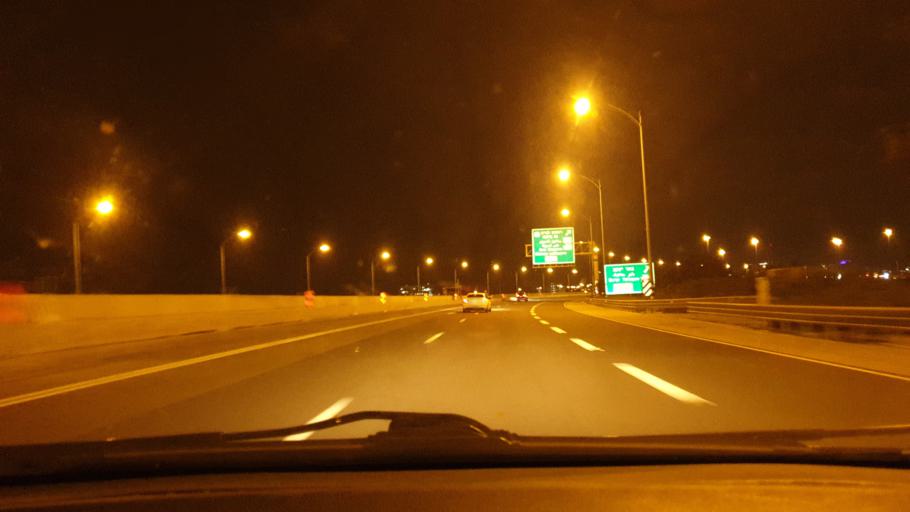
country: IL
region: Central District
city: Ness Ziona
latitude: 31.9301
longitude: 34.8207
